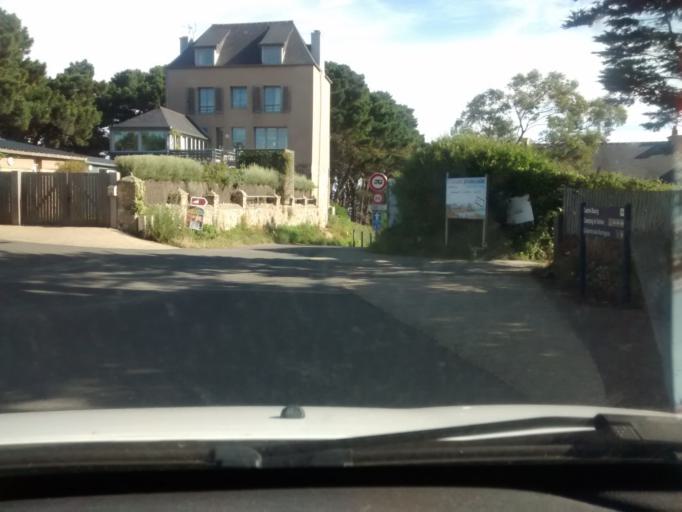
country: FR
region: Brittany
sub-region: Departement des Cotes-d'Armor
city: Plougrescant
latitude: 48.8622
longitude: -3.2192
